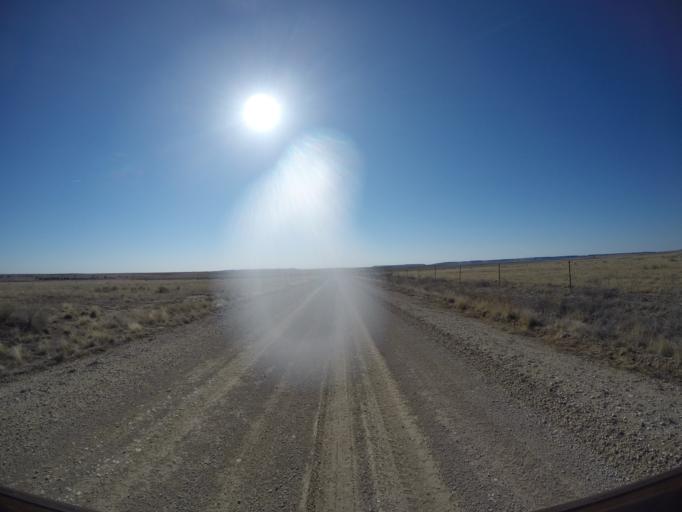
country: US
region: Colorado
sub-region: Otero County
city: La Junta
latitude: 37.6945
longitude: -103.6204
